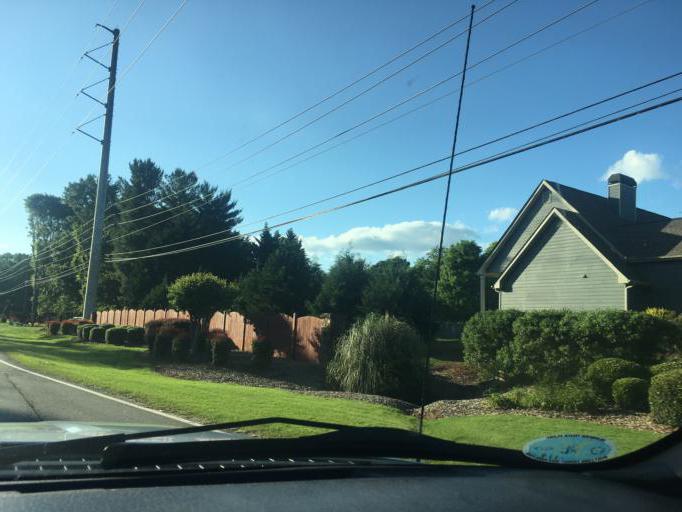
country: US
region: Georgia
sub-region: Forsyth County
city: Cumming
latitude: 34.2811
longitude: -84.1206
